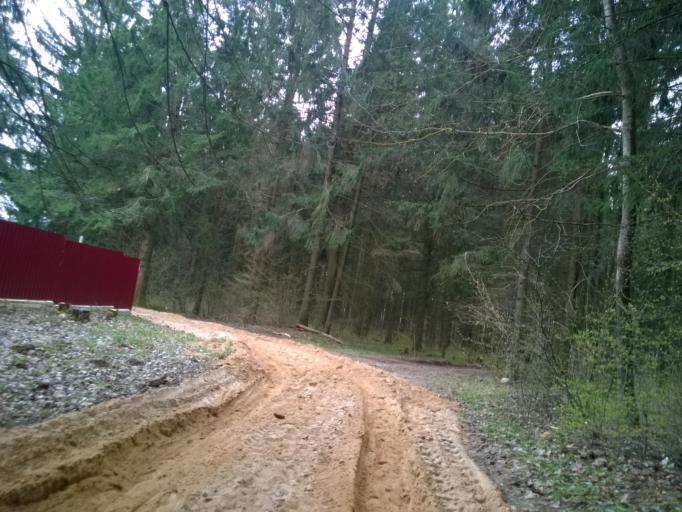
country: BY
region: Minsk
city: Slabada
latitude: 54.0047
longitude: 27.8474
